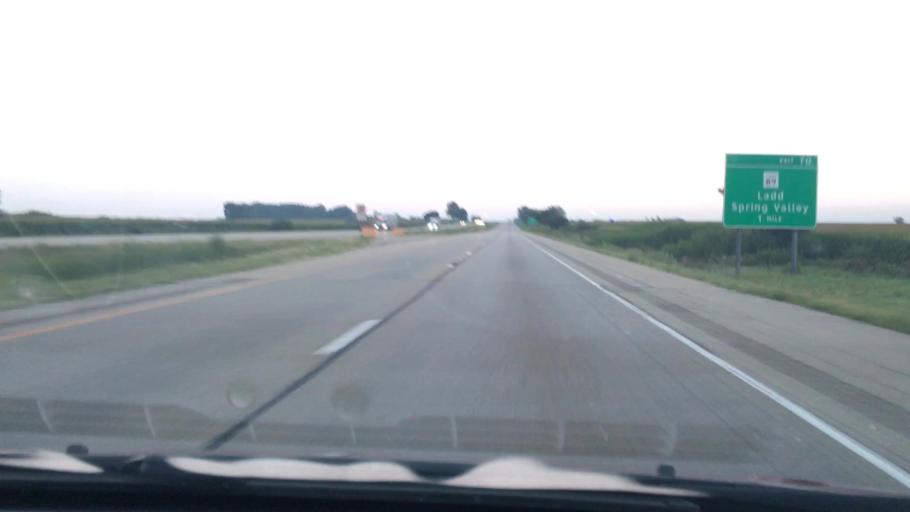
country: US
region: Illinois
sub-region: Bureau County
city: Ladd
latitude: 41.3711
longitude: -89.2389
